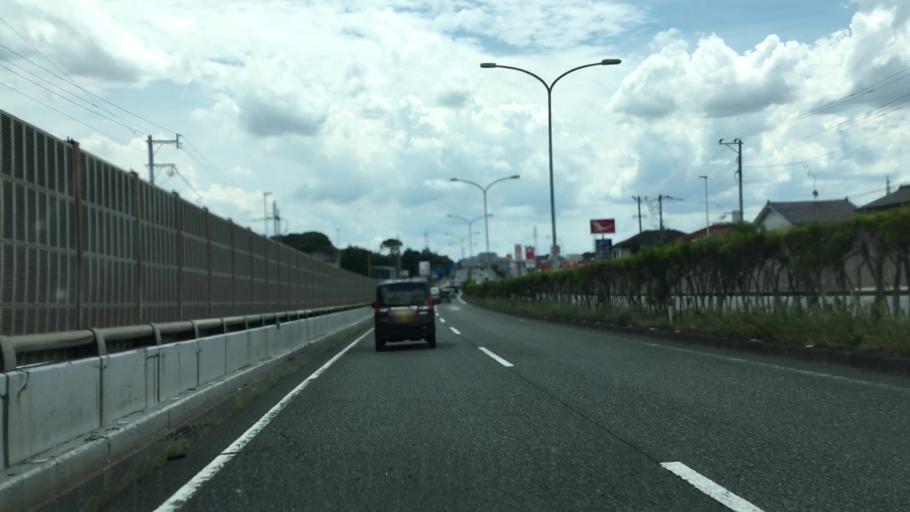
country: JP
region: Fukuoka
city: Chikushino-shi
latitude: 33.4813
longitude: 130.5386
